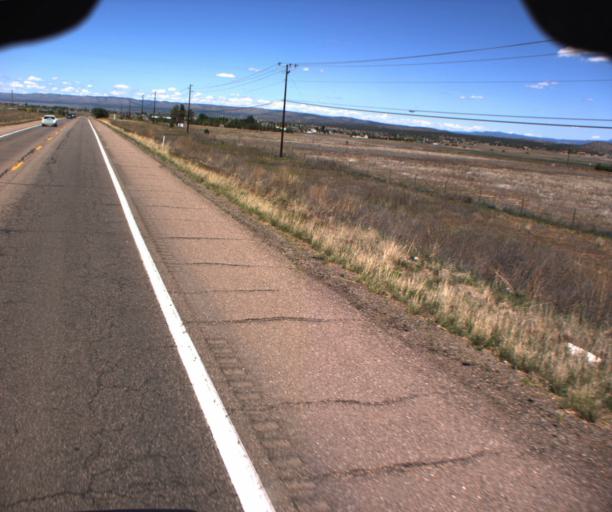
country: US
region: Arizona
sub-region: Yavapai County
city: Paulden
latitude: 34.8353
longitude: -112.4615
